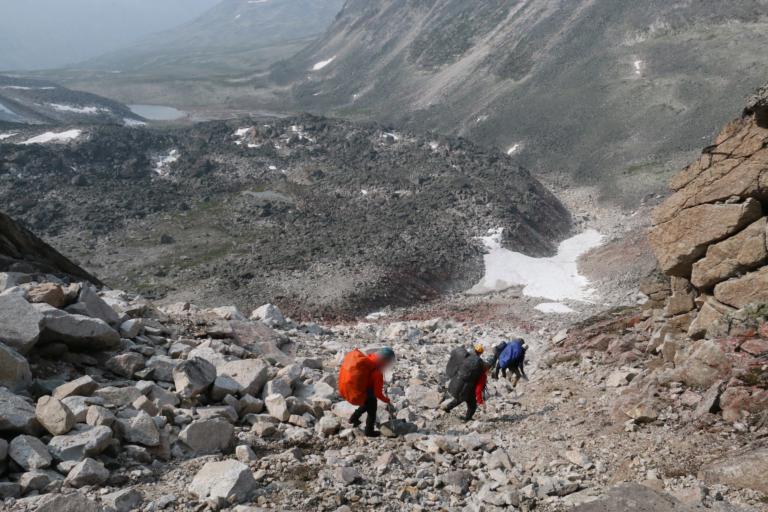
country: RU
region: Respublika Buryatiya
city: Novyy Uoyan
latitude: 56.2179
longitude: 110.9996
